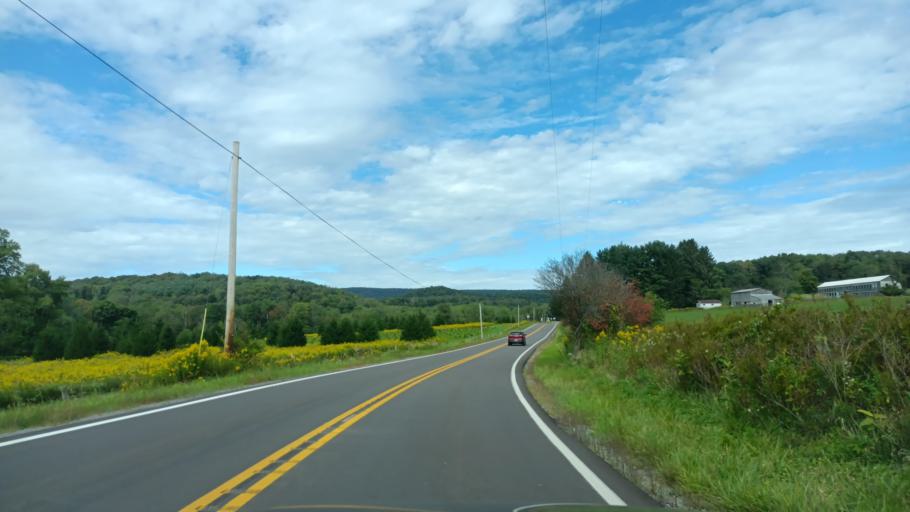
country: US
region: Maryland
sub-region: Garrett County
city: Oakland
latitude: 39.3127
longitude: -79.4820
